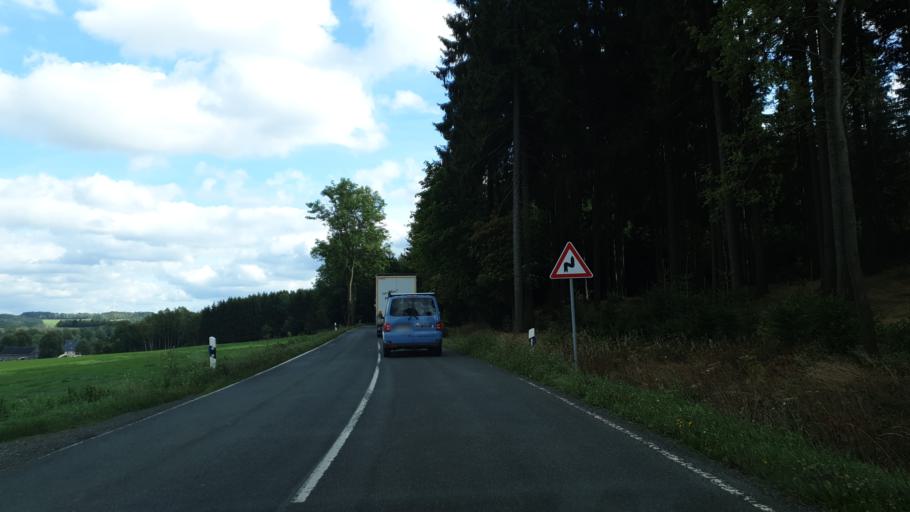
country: DE
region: Saxony
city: Lossnitz
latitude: 50.6501
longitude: 12.7195
